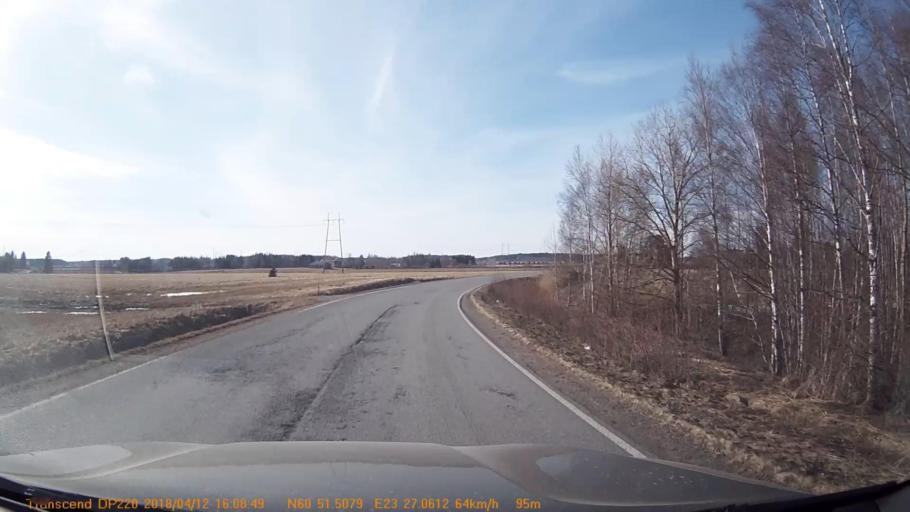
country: FI
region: Haeme
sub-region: Forssa
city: Jokioinen
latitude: 60.8580
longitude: 23.4519
